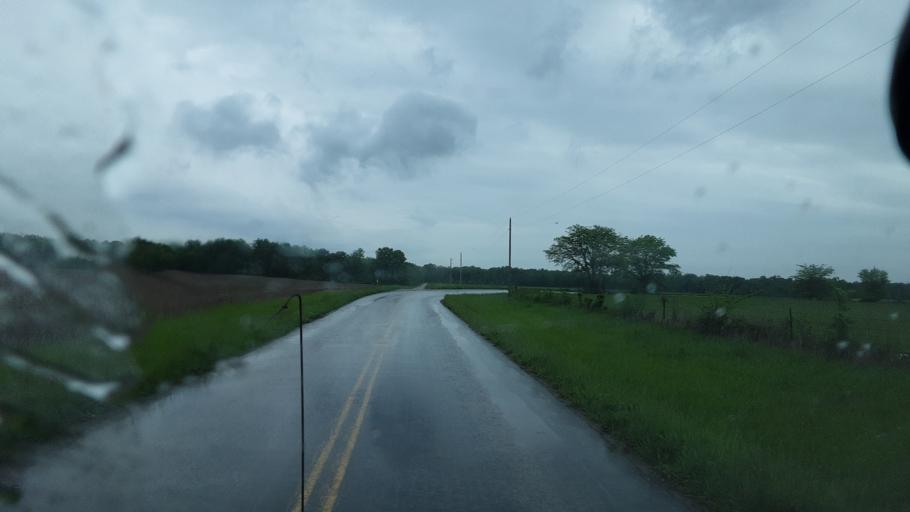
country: US
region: Missouri
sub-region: Boone County
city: Centralia
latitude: 39.3696
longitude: -92.2492
